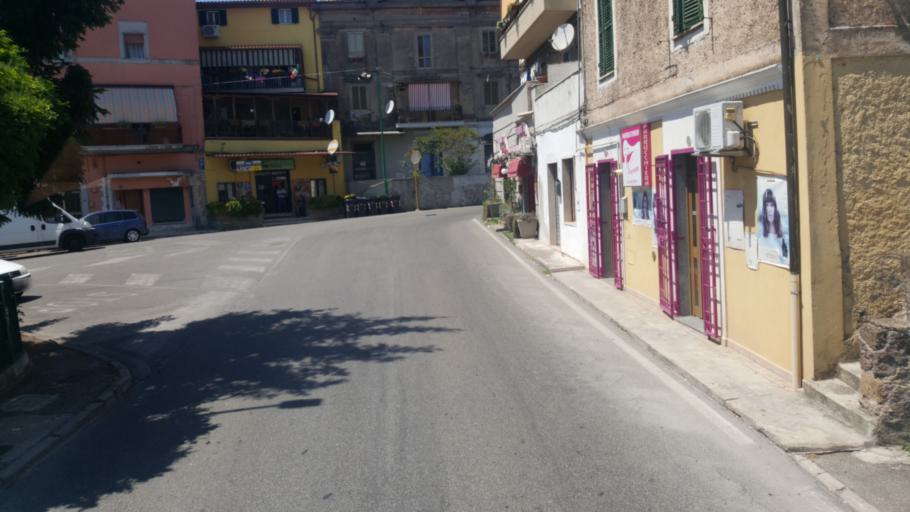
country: IT
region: Latium
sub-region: Citta metropolitana di Roma Capitale
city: Colleferro
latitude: 41.7405
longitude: 13.0015
